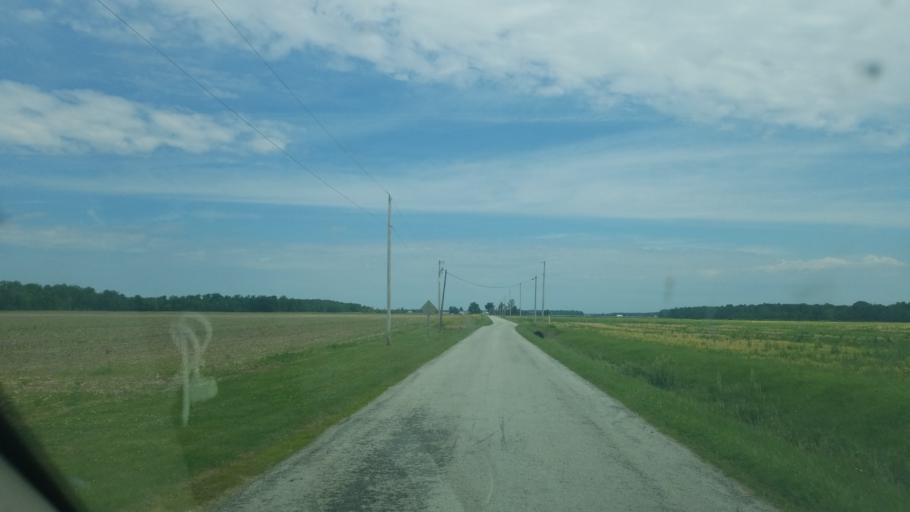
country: US
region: Ohio
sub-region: Wood County
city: North Baltimore
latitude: 41.2110
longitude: -83.5732
